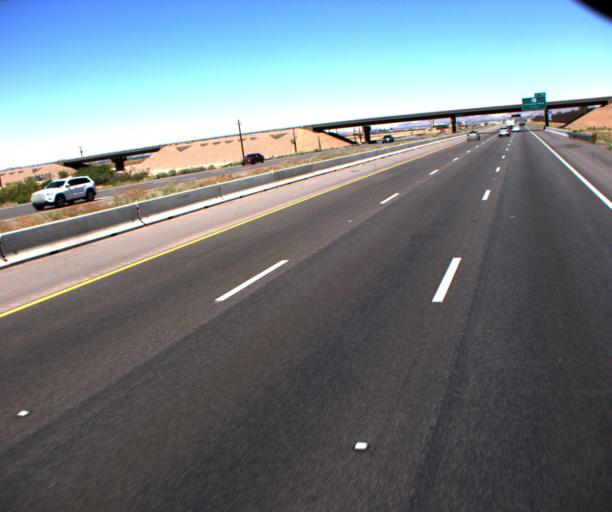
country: US
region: Arizona
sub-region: Pinal County
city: Casa Grande
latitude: 32.8636
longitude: -111.6869
